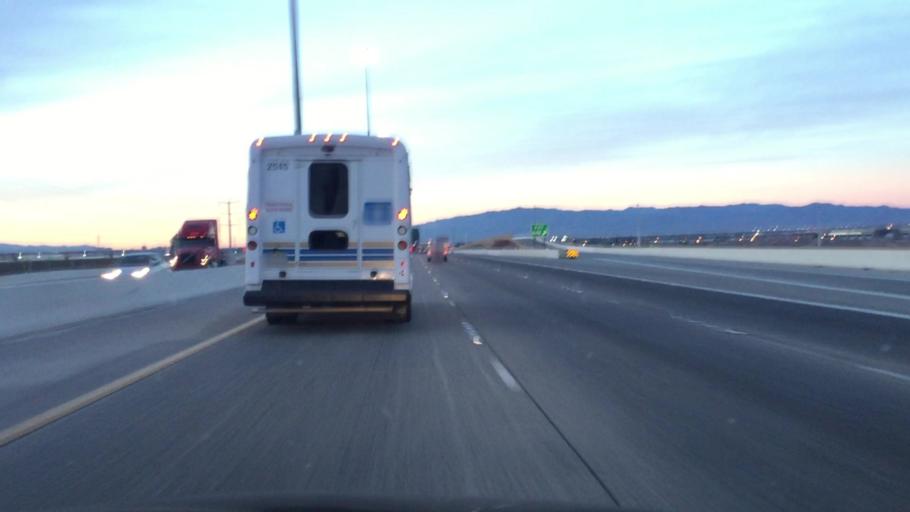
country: US
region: Nevada
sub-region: Clark County
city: Whitney
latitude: 36.0623
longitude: -115.0309
